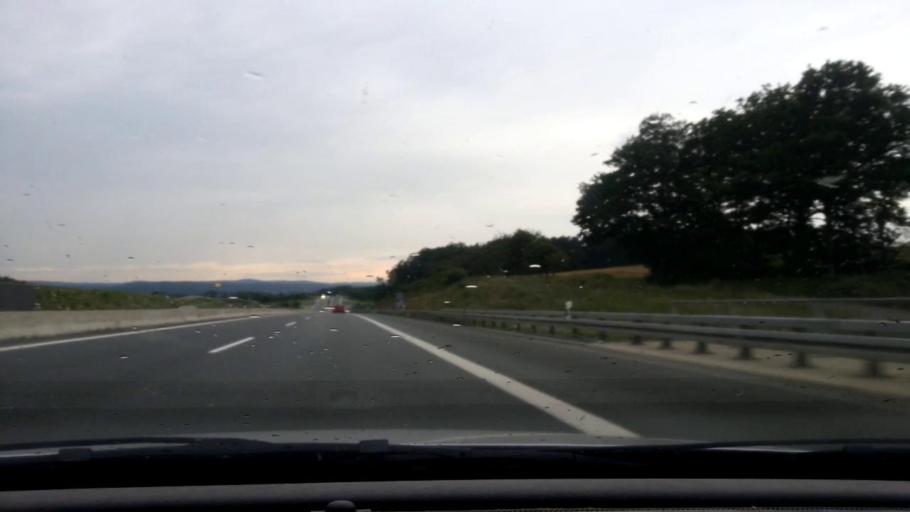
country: DE
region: Bavaria
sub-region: Upper Franconia
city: Neudrossenfeld
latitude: 50.0403
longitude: 11.5025
